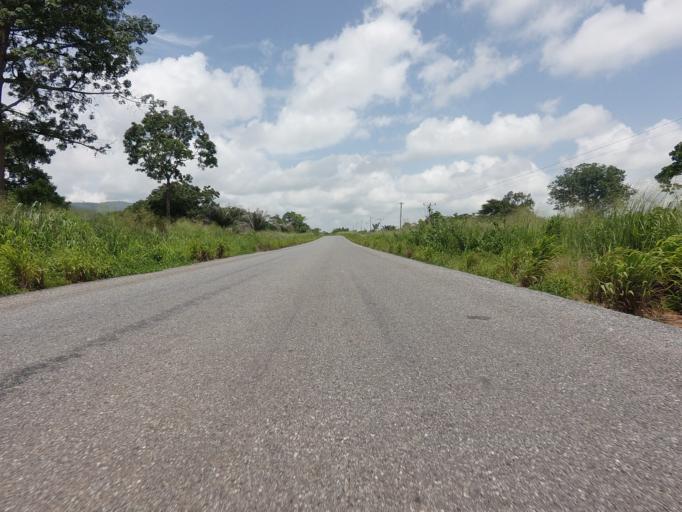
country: GH
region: Volta
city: Kpandu
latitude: 6.8582
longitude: 0.3953
